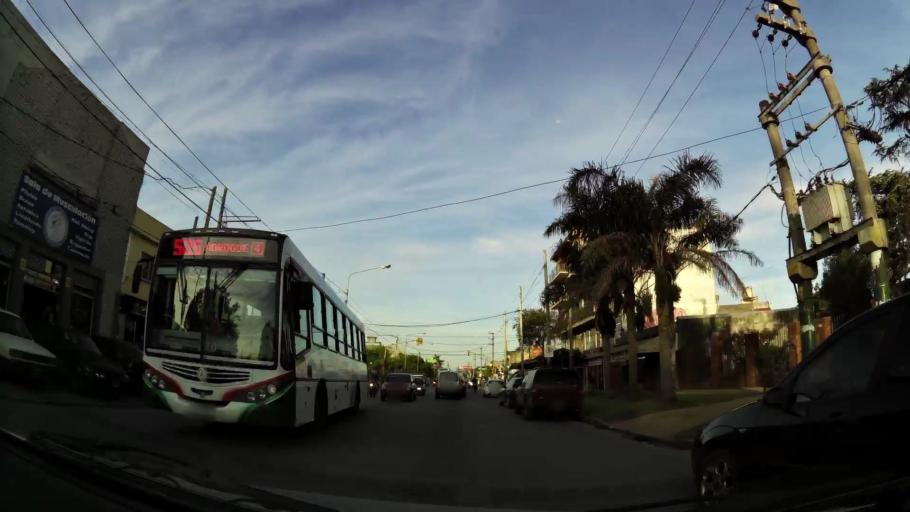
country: AR
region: Buenos Aires
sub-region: Partido de Almirante Brown
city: Adrogue
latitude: -34.7940
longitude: -58.3613
